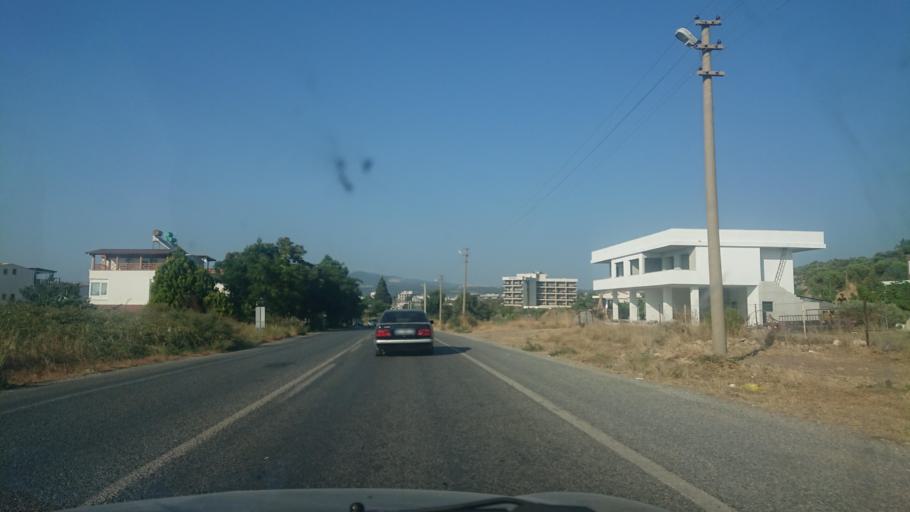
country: TR
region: Aydin
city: Davutlar
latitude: 37.7278
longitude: 27.2662
